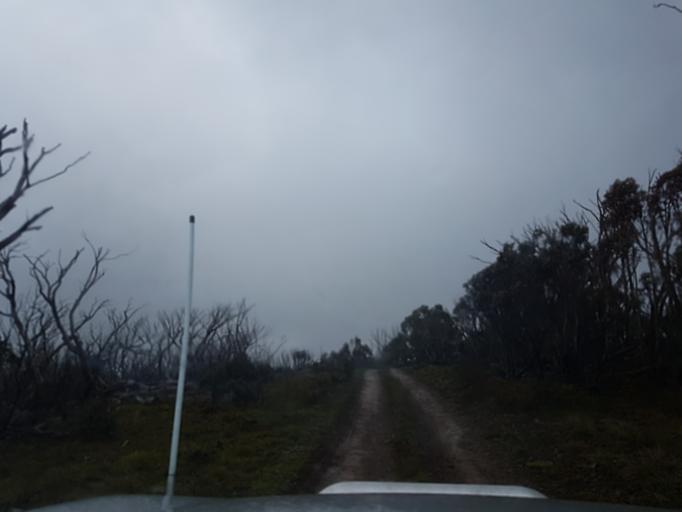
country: AU
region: Victoria
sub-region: Alpine
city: Mount Beauty
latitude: -37.0940
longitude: 147.0621
